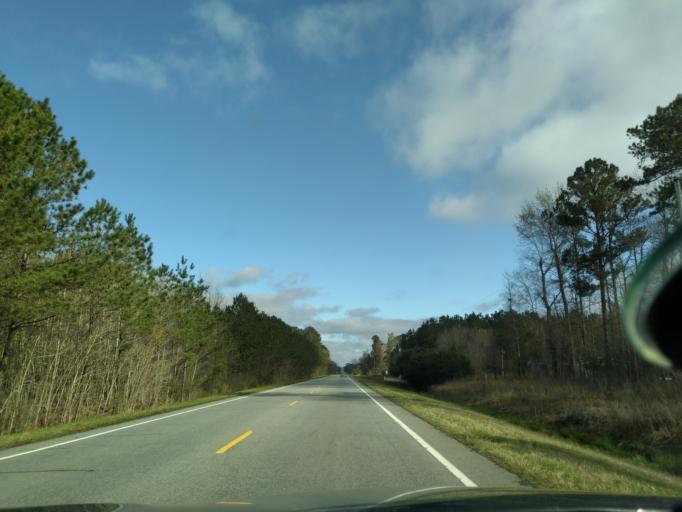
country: US
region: North Carolina
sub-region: Washington County
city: Plymouth
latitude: 36.0030
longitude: -76.7737
